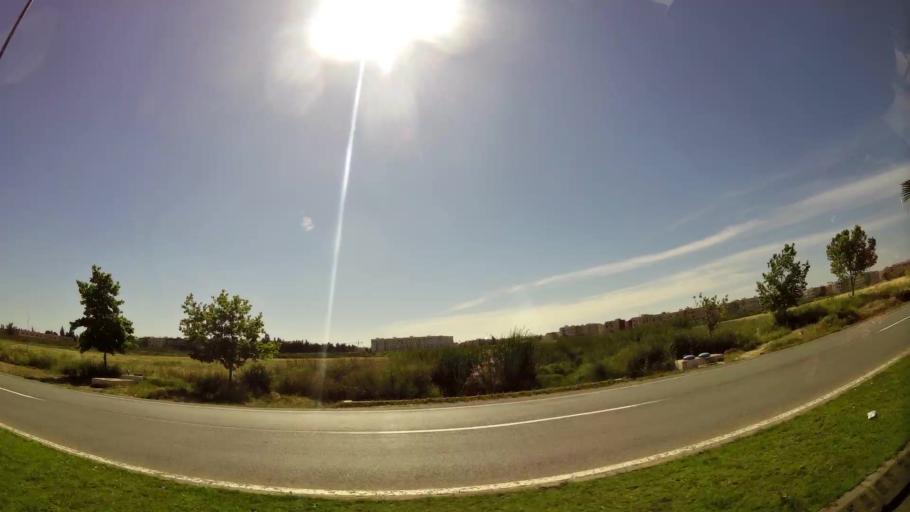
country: MA
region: Fes-Boulemane
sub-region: Fes
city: Fes
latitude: 34.0135
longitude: -5.0199
